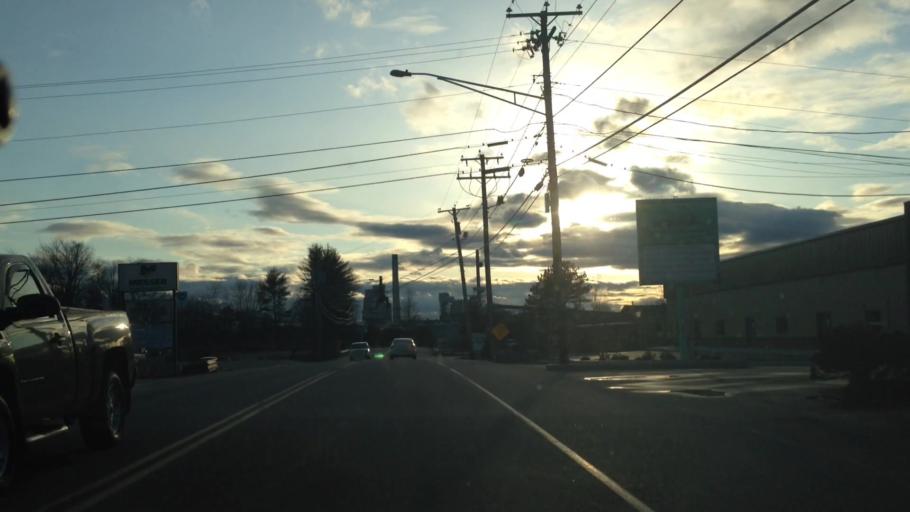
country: US
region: Maine
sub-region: Cumberland County
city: Westbrook
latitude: 43.6854
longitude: -70.3399
